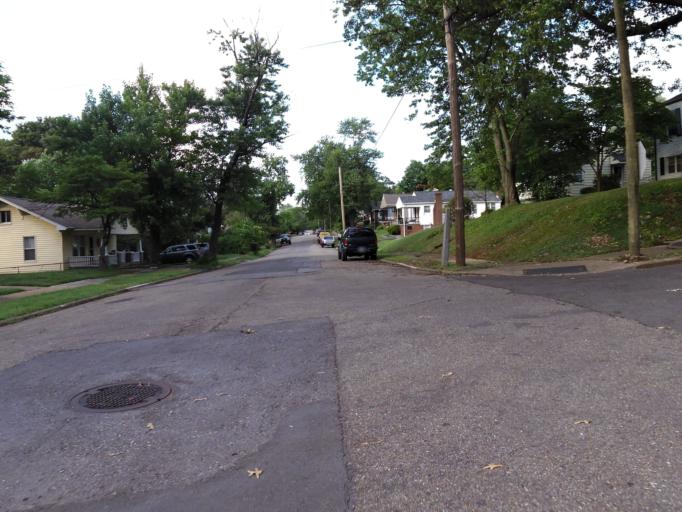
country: US
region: Tennessee
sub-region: Knox County
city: Knoxville
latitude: 35.9898
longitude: -83.9344
